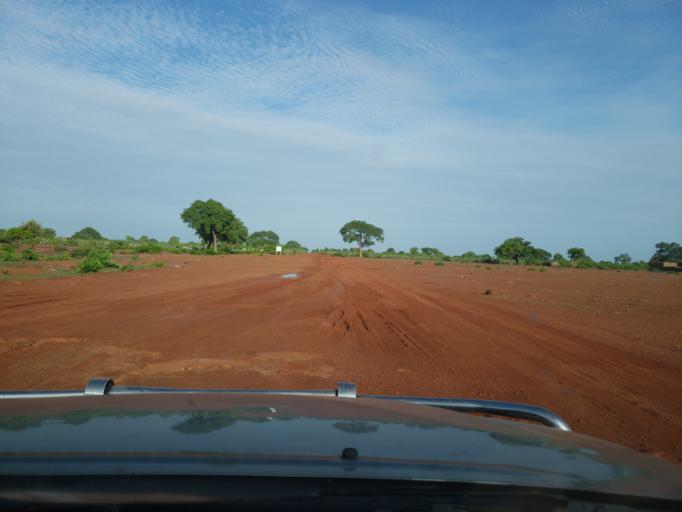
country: ML
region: Sikasso
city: Koutiala
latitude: 12.4285
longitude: -5.6235
